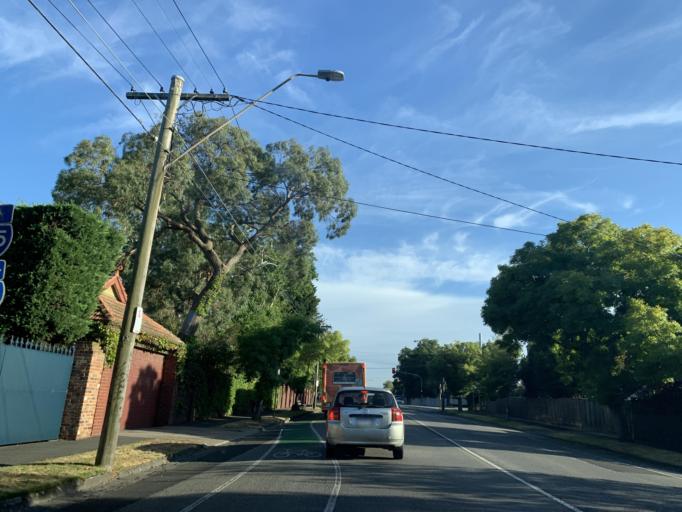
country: AU
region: Victoria
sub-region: Bayside
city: North Brighton
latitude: -37.8991
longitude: 144.9941
